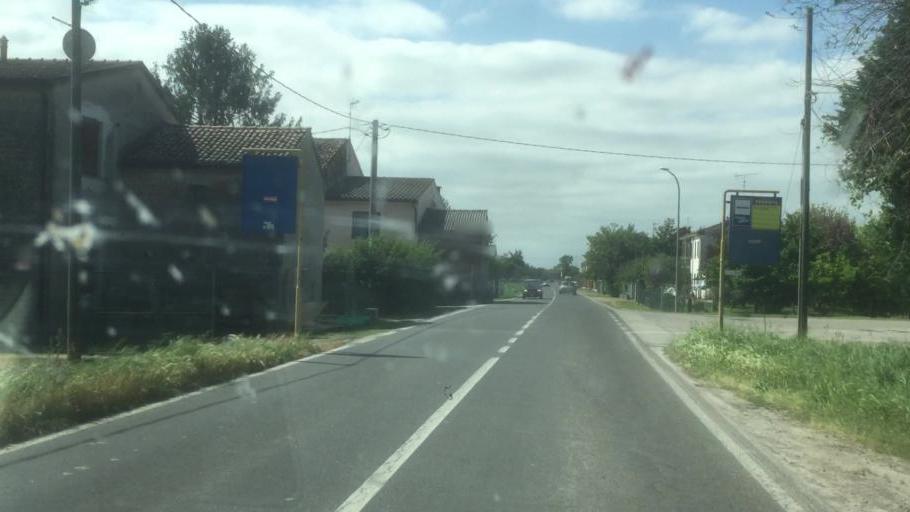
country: IT
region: Veneto
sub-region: Provincia di Rovigo
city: Ceneselli
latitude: 45.0152
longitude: 11.3784
